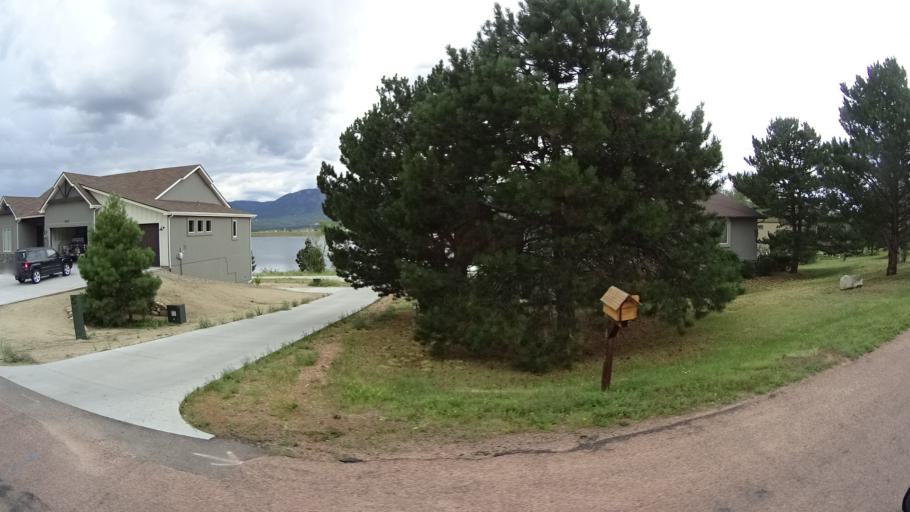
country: US
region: Colorado
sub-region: El Paso County
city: Woodmoor
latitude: 39.1009
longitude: -104.8537
